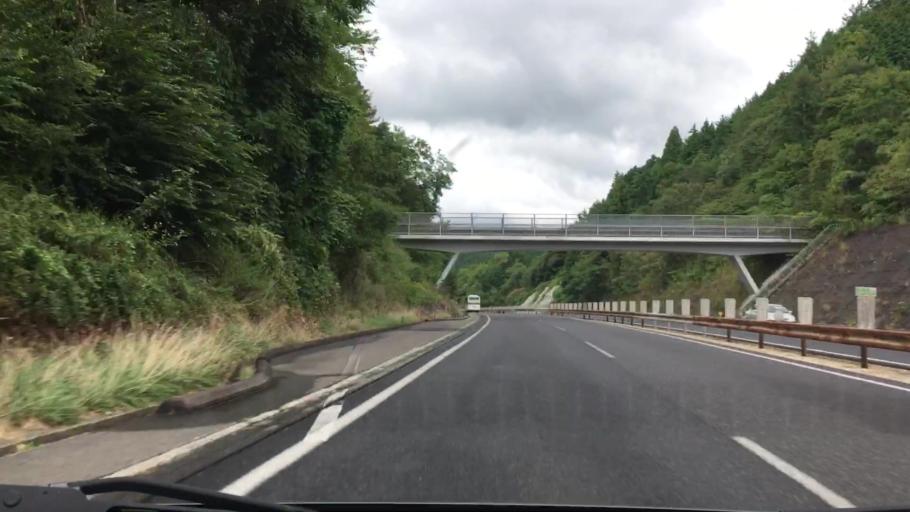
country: JP
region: Okayama
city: Takahashi
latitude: 35.0019
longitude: 133.7258
